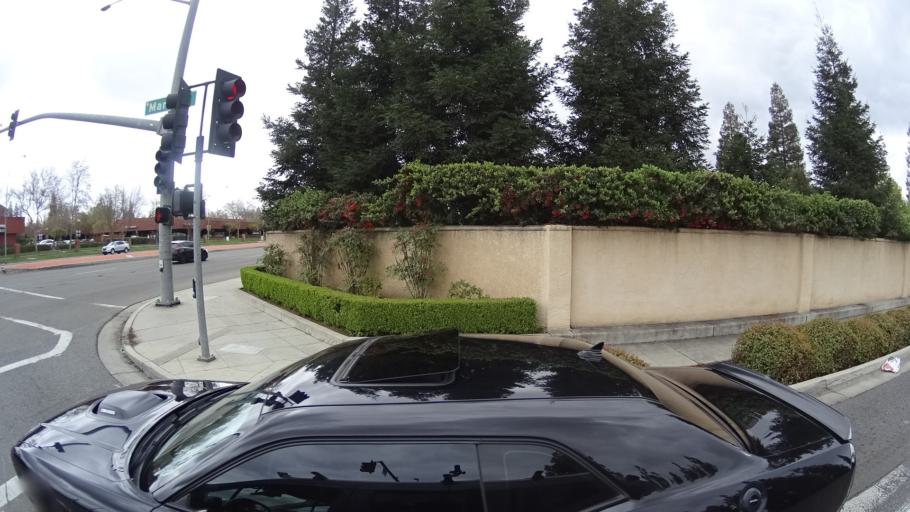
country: US
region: California
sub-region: Fresno County
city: Fresno
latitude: 36.8370
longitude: -119.8474
